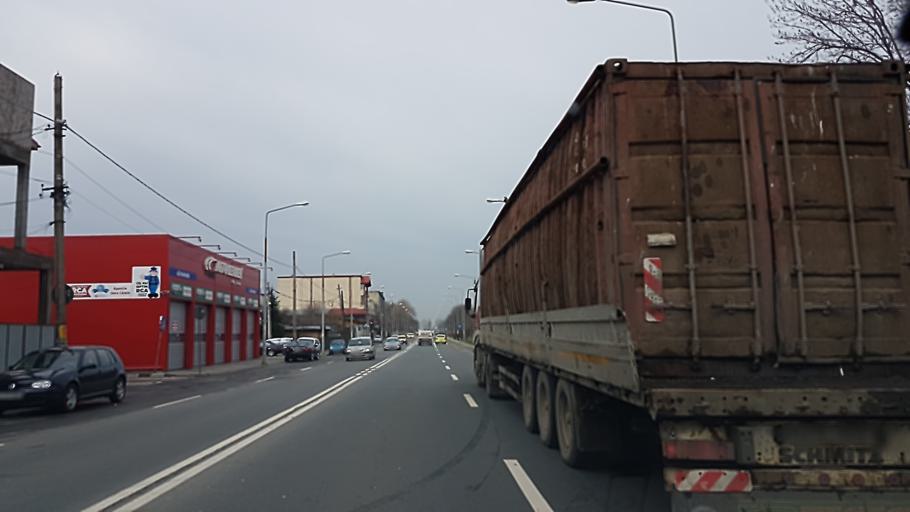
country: RO
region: Ilfov
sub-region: Comuna Pantelimon
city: Pantelimon
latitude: 44.4372
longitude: 26.1990
